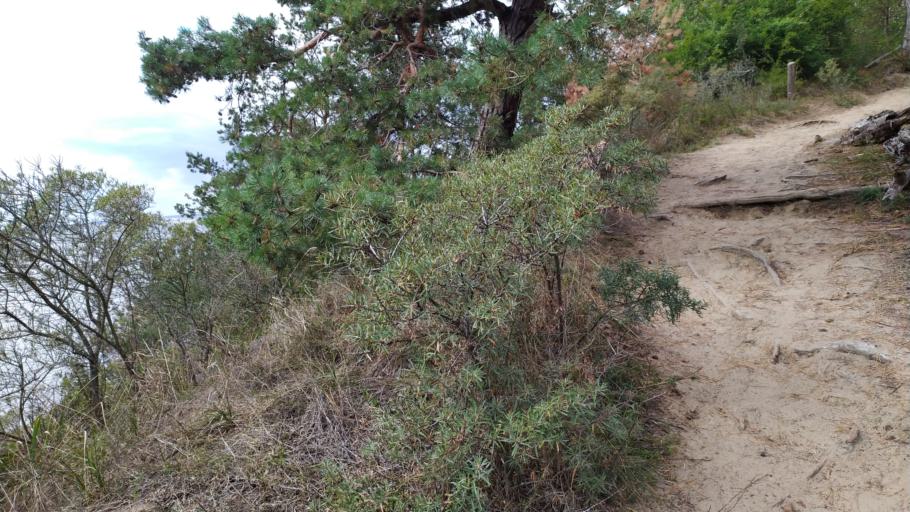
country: DE
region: Mecklenburg-Vorpommern
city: Lassan
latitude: 54.0028
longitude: 13.8553
